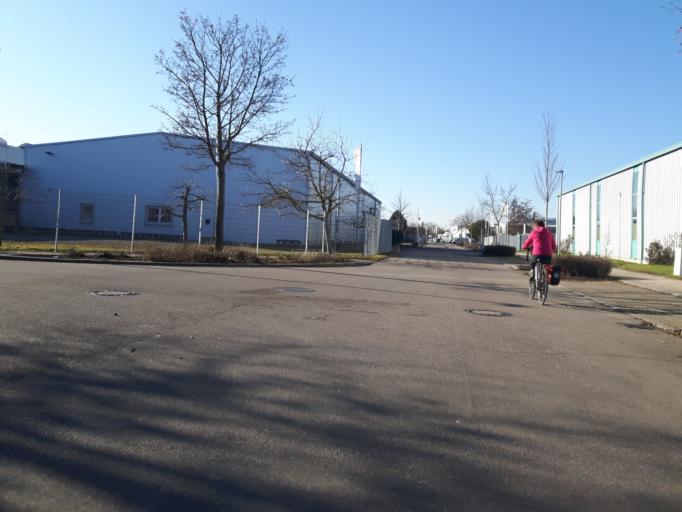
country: DE
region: Baden-Wuerttemberg
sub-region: Regierungsbezirk Stuttgart
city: Brackenheim
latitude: 49.0670
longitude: 9.0721
